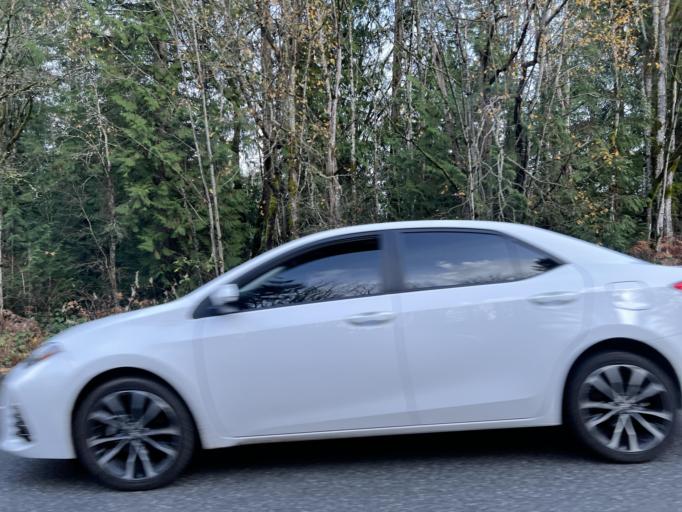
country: US
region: Washington
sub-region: Kitsap County
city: Bainbridge Island
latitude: 47.6461
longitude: -122.5194
